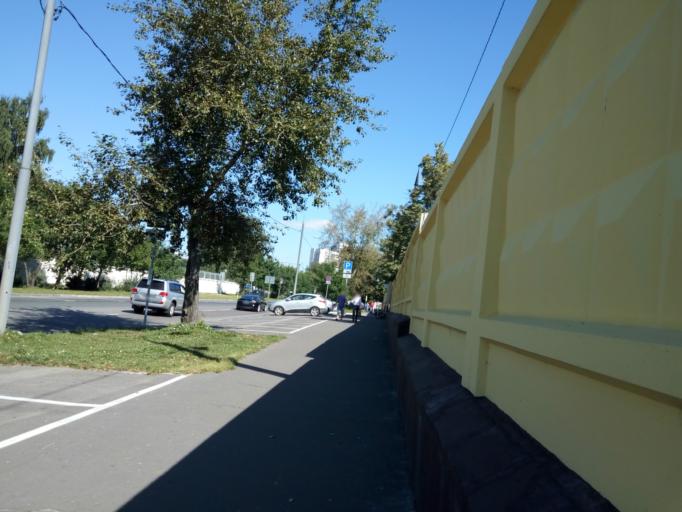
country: RU
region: Moscow
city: Sokol
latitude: 55.7730
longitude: 37.5191
